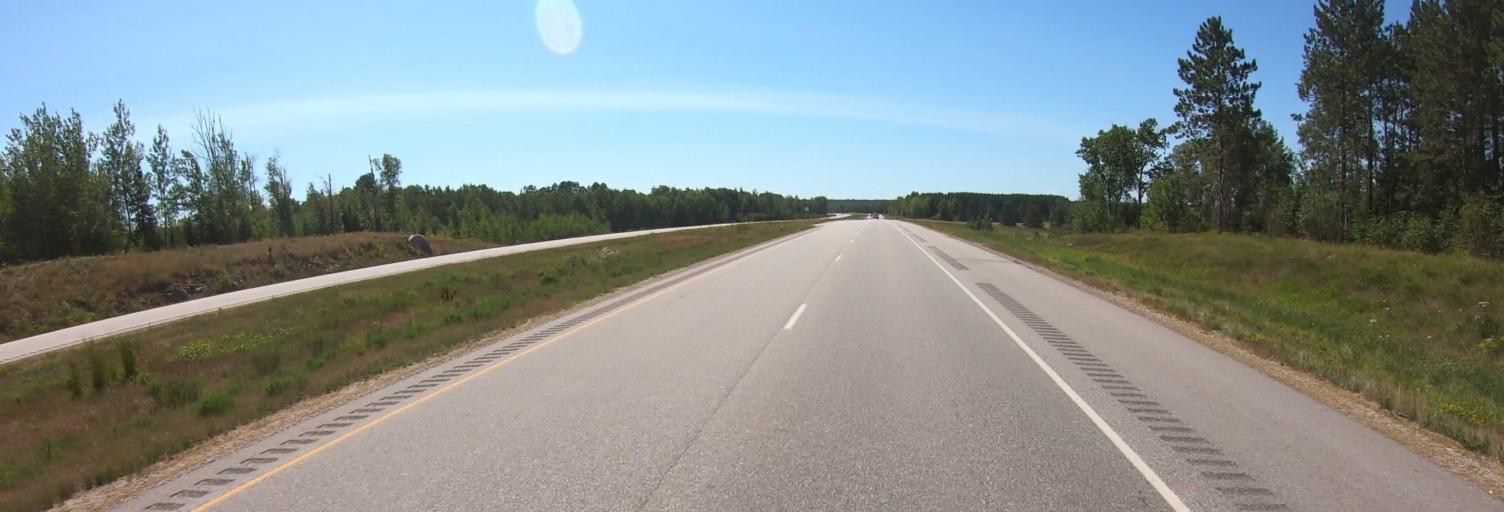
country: US
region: Minnesota
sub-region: Saint Louis County
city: Mountain Iron
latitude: 47.7272
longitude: -92.6516
